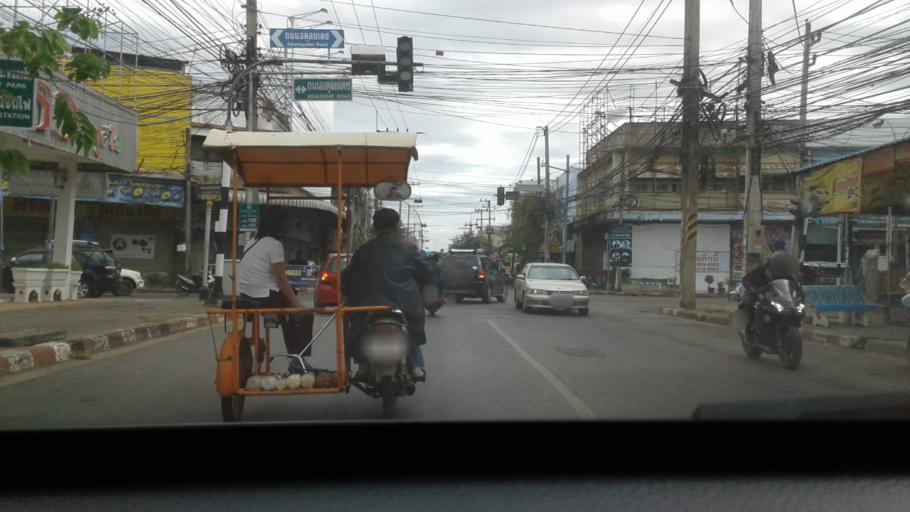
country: TH
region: Changwat Udon Thani
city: Udon Thani
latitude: 17.4094
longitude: 102.7996
